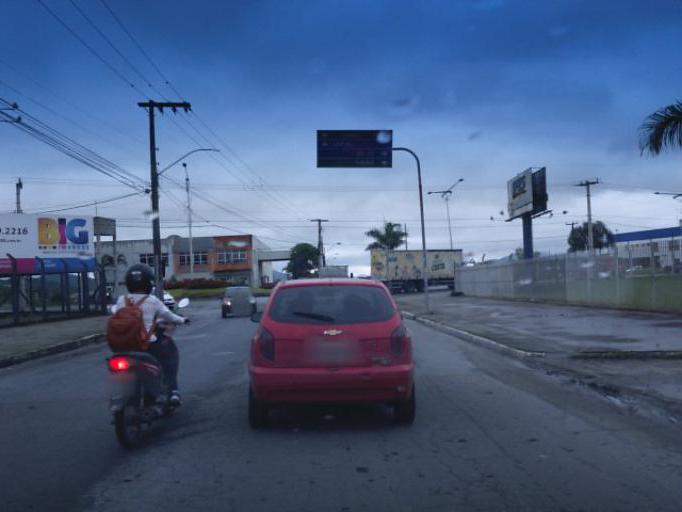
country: BR
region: Santa Catarina
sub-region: Itajai
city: Itajai
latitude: -26.9152
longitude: -48.7008
